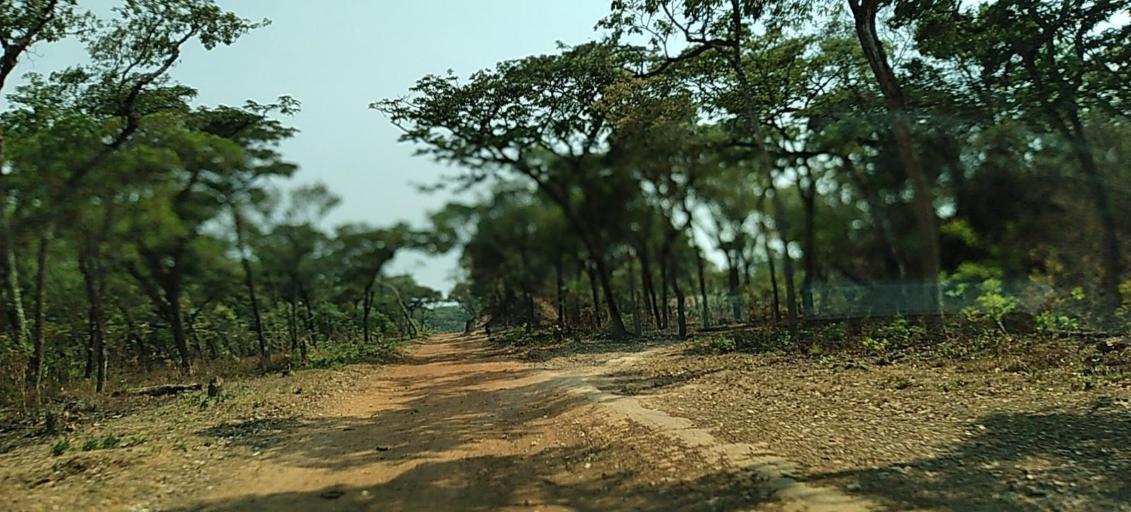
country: ZM
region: North-Western
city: Kansanshi
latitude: -12.0712
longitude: 26.8882
